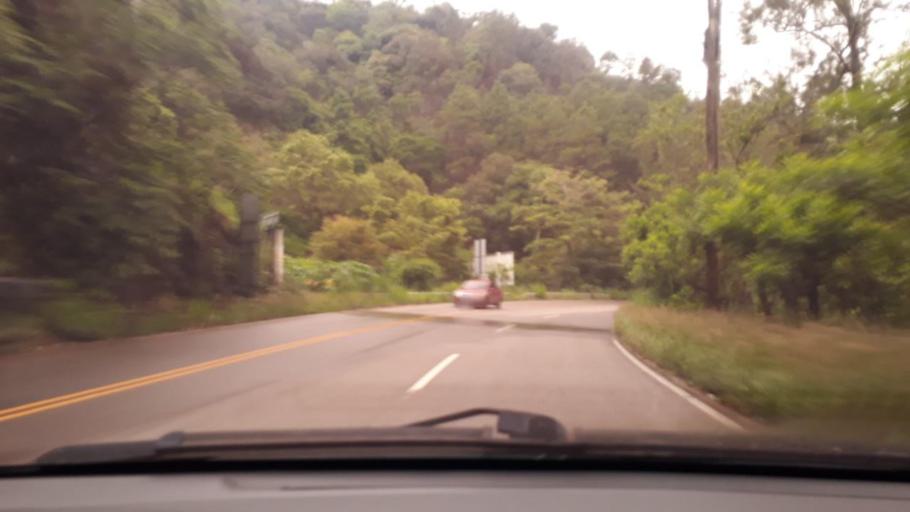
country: GT
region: Chiquimula
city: Esquipulas
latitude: 14.5639
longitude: -89.3616
